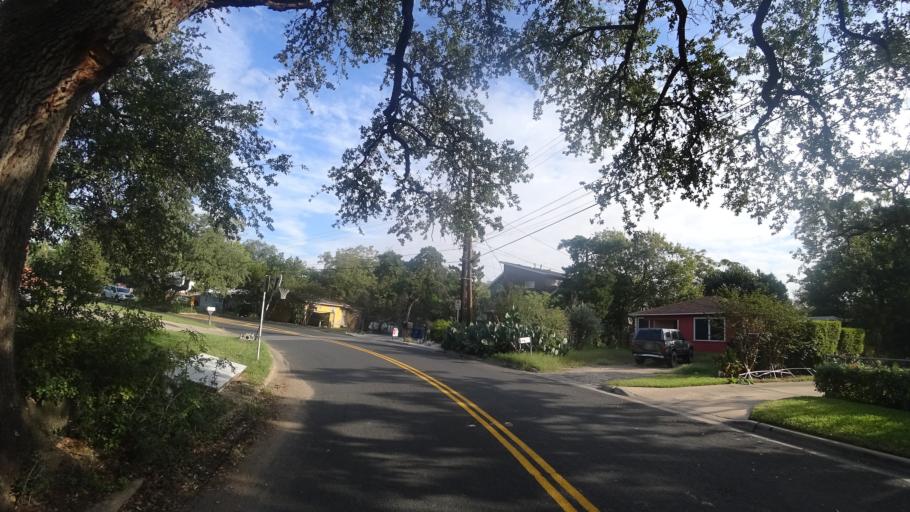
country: US
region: Texas
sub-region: Travis County
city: Austin
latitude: 30.2740
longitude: -97.7024
